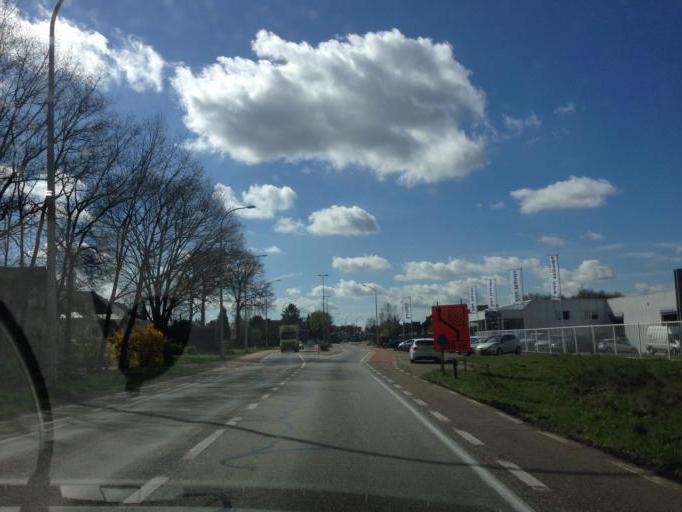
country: BE
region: Flanders
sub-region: Provincie Limburg
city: Helchteren
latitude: 51.0646
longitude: 5.3829
